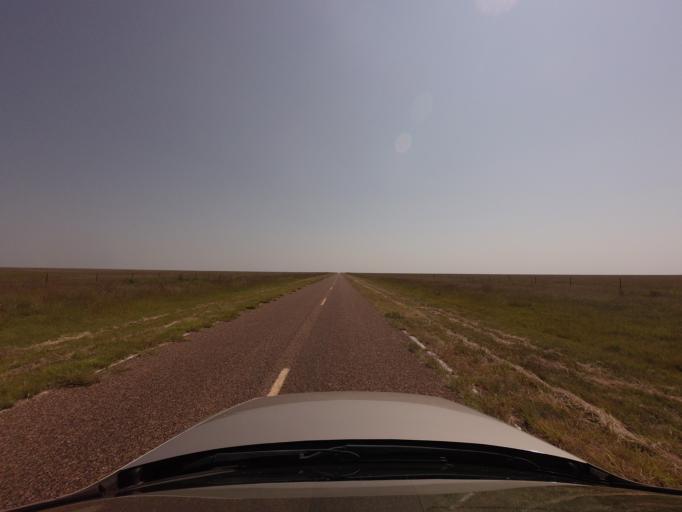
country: US
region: New Mexico
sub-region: Curry County
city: Cannon Air Force Base
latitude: 34.6333
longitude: -103.4489
